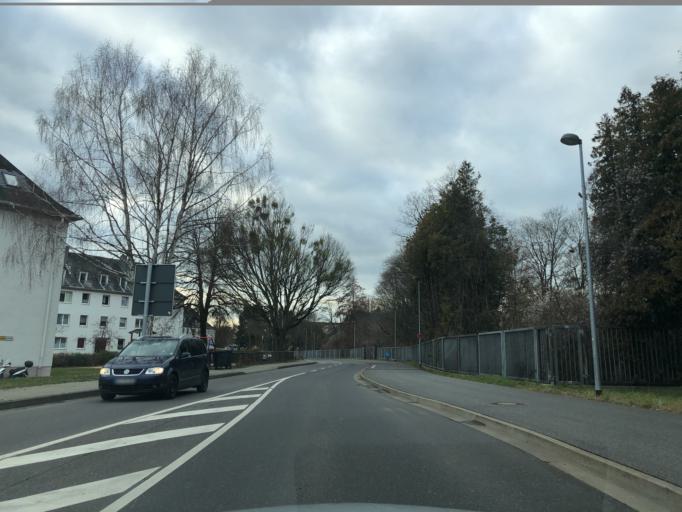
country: DE
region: Rheinland-Pfalz
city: Urbar
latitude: 50.3734
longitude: 7.6316
